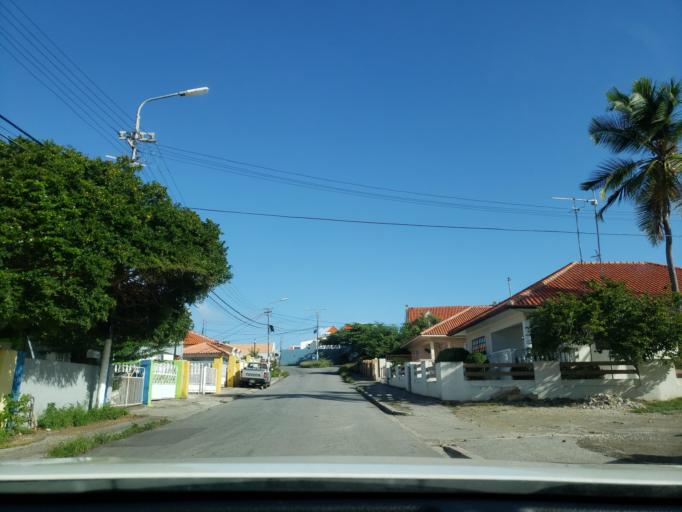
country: CW
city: Willemstad
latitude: 12.1022
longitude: -68.9183
